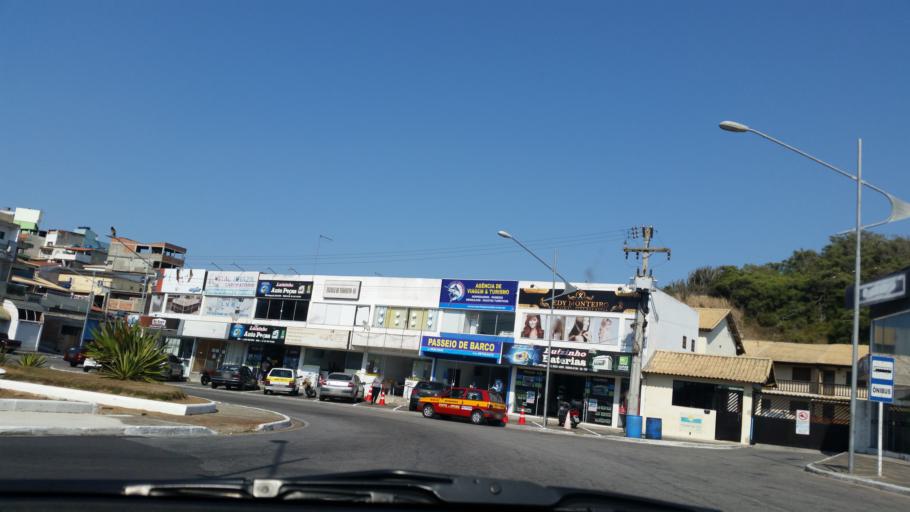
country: BR
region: Rio de Janeiro
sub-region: Arraial Do Cabo
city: Arraial do Cabo
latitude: -22.9649
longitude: -42.0294
